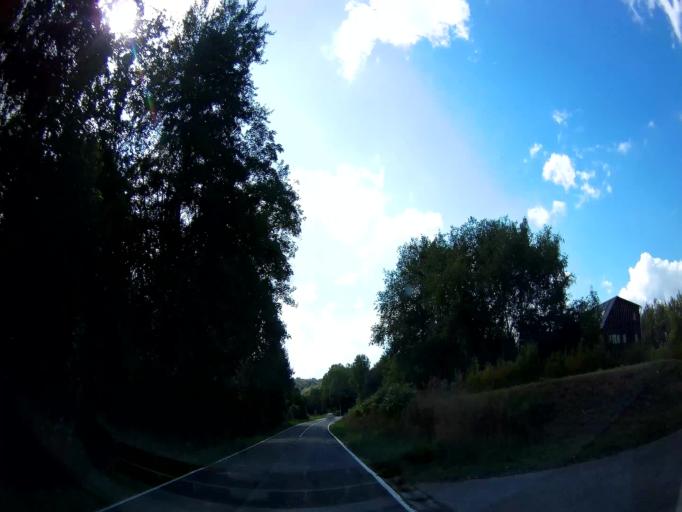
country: BE
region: Wallonia
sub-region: Province de Namur
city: Anhee
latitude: 50.3172
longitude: 4.8503
